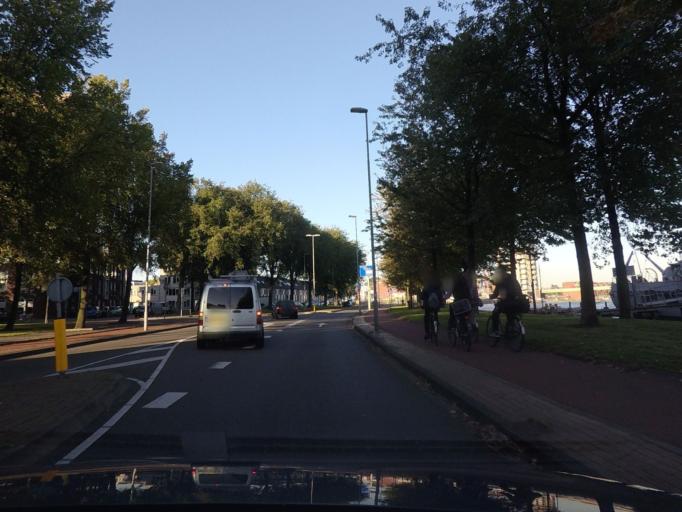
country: NL
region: North Holland
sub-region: Gemeente Haarlem
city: Haarlem
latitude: 52.4019
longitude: 4.6532
